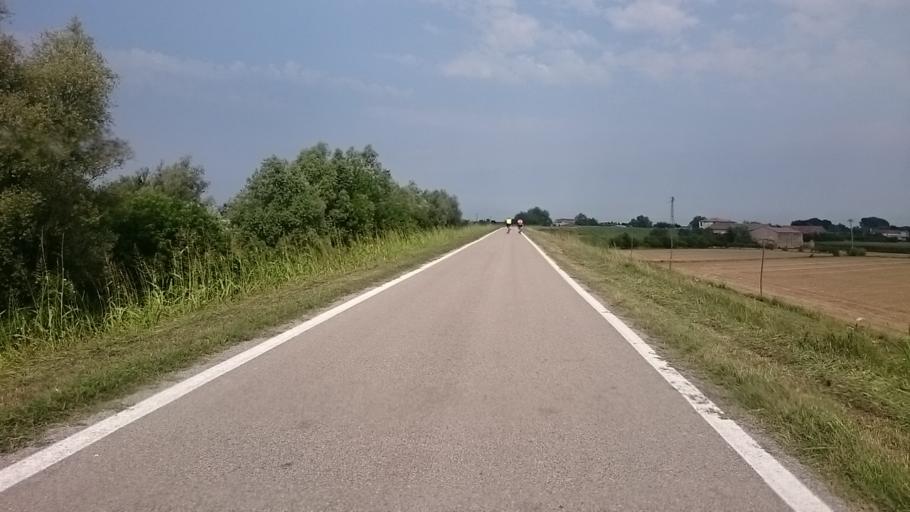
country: IT
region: Veneto
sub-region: Provincia di Padova
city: Bovolenta
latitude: 45.2744
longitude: 11.9366
